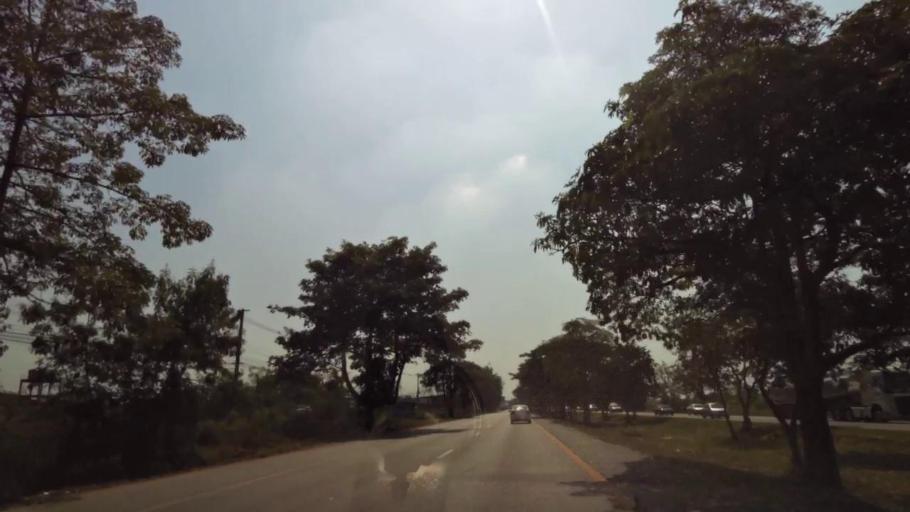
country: TH
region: Phichit
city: Wachira Barami
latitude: 16.5171
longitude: 100.1429
